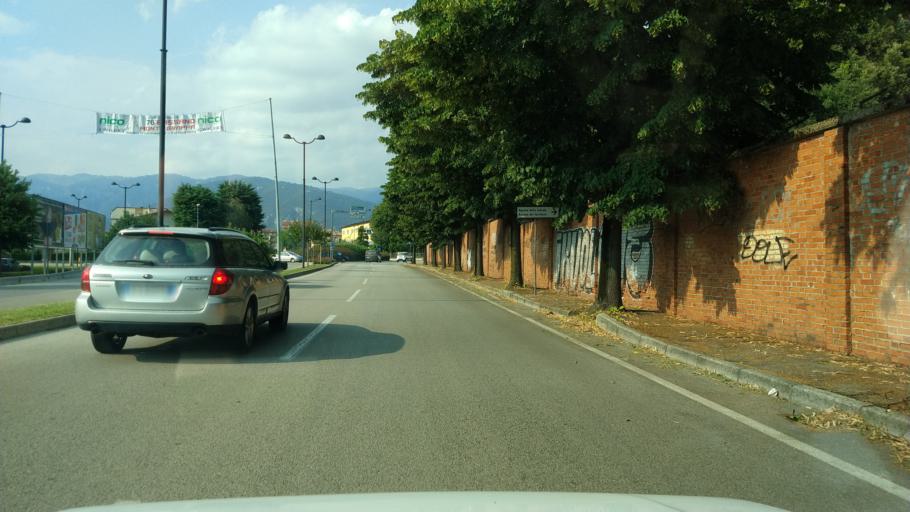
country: IT
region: Veneto
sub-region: Provincia di Vicenza
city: Bassano del Grappa
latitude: 45.7595
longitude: 11.7315
